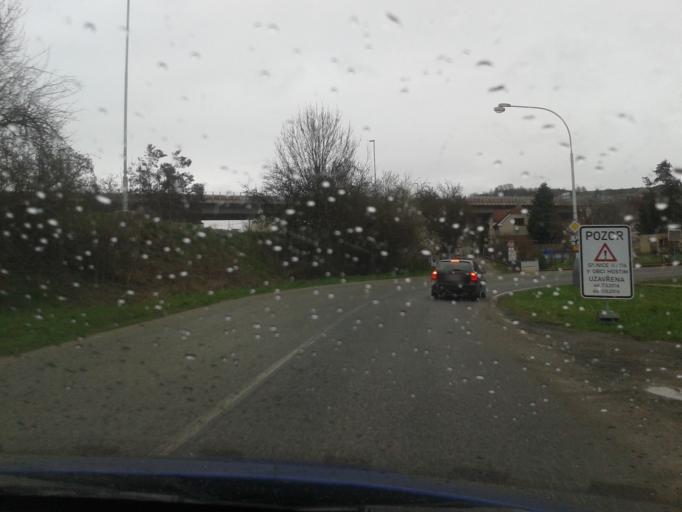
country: CZ
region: Central Bohemia
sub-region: Okres Beroun
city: Beroun
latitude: 49.9615
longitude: 14.0886
